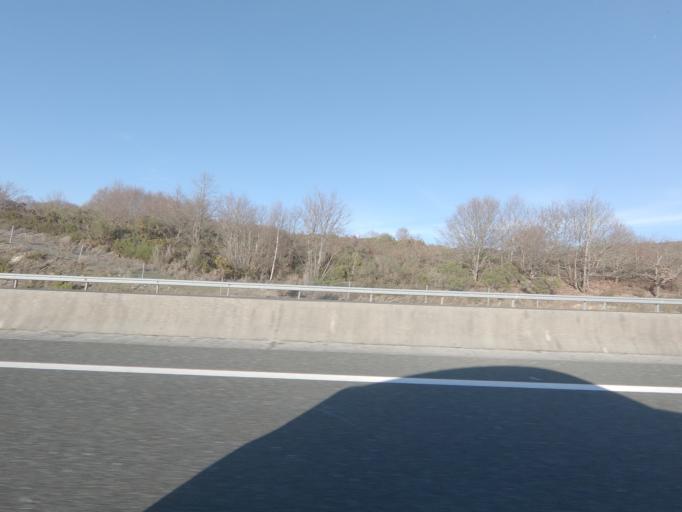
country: ES
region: Galicia
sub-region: Provincia de Pontevedra
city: Dozon
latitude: 42.5862
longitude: -8.0738
